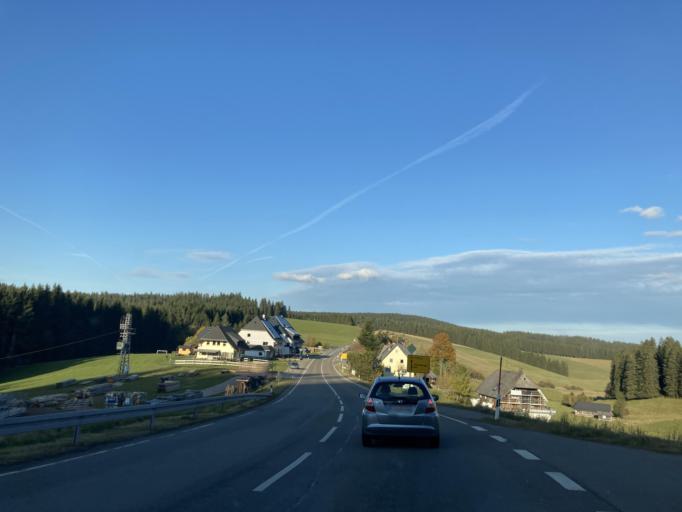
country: DE
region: Baden-Wuerttemberg
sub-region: Freiburg Region
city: Furtwangen im Schwarzwald
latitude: 47.9982
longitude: 8.1946
